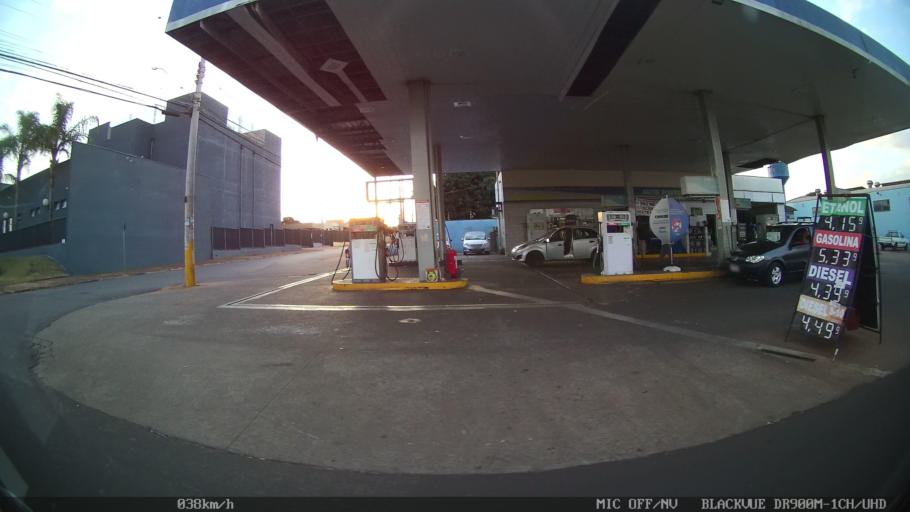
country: BR
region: Sao Paulo
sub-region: Ribeirao Preto
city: Ribeirao Preto
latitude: -21.1357
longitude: -47.8183
